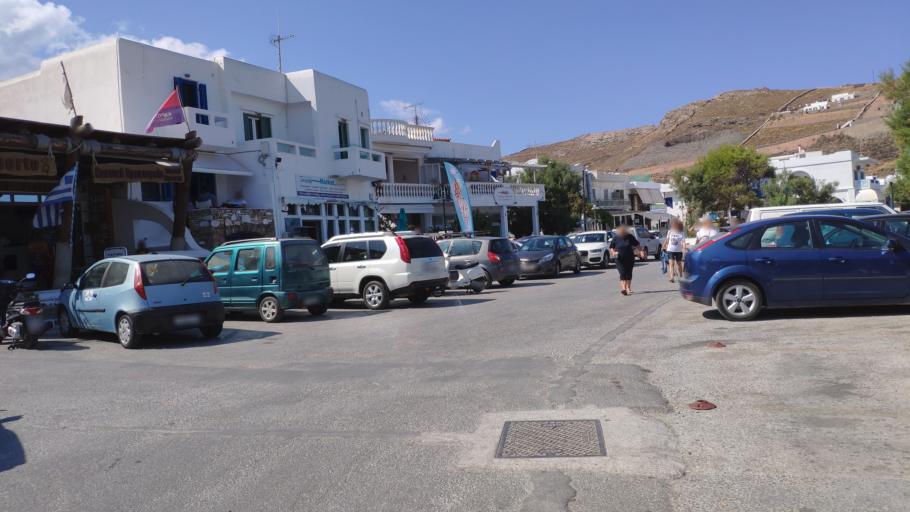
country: GR
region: South Aegean
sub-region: Nomos Kykladon
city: Kythnos
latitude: 37.3890
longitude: 24.3980
